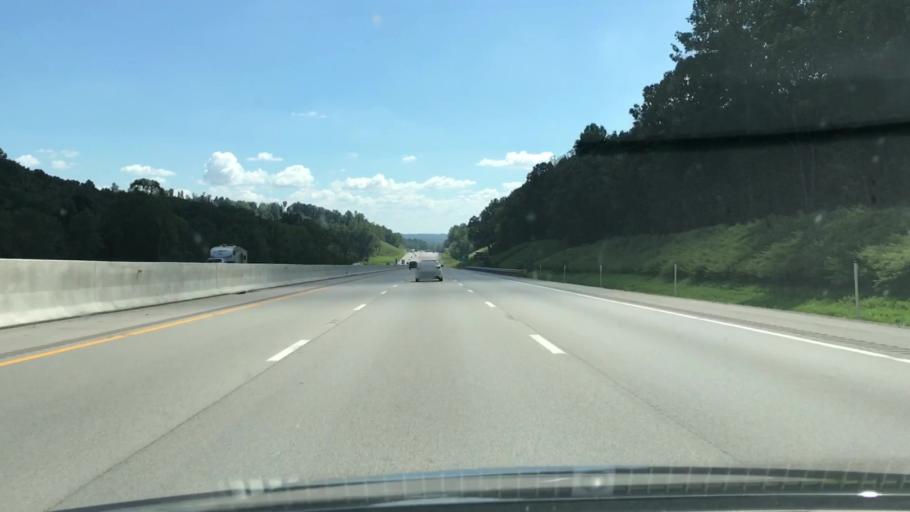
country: US
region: Kentucky
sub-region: Hart County
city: Munfordville
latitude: 37.3176
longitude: -85.9055
